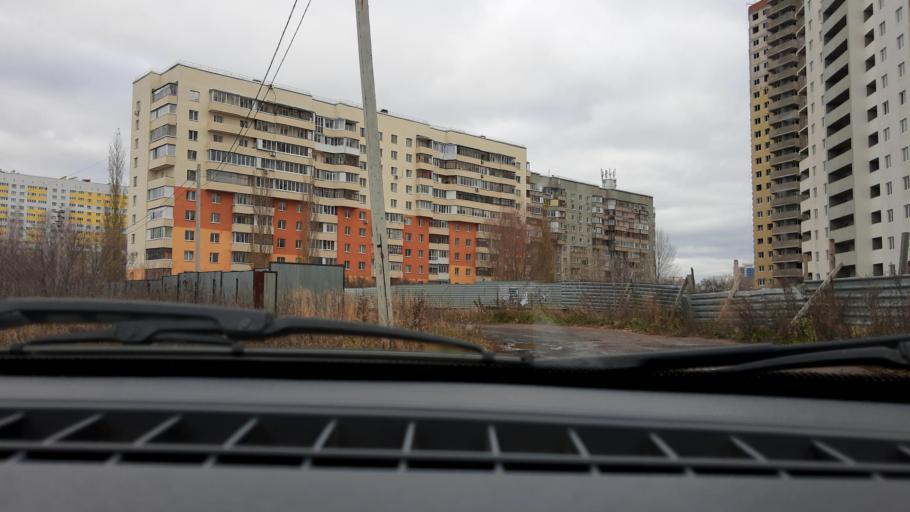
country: RU
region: Bashkortostan
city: Mikhaylovka
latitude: 54.7889
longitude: 55.8675
